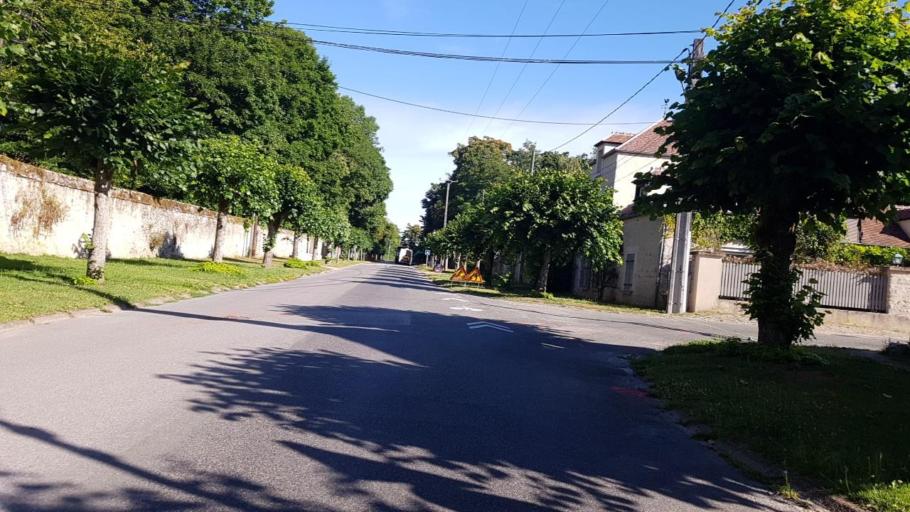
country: FR
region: Picardie
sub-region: Departement de l'Oise
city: Chamant
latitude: 49.2252
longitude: 2.6061
